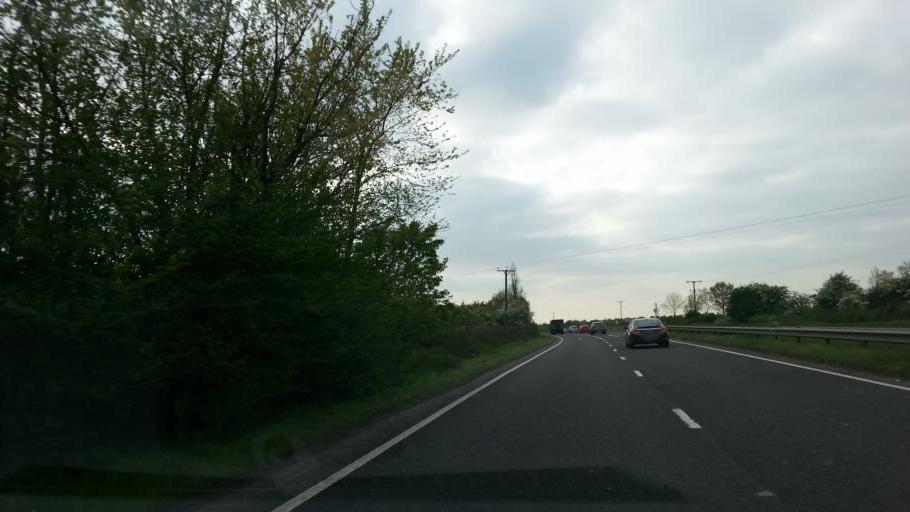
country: GB
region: England
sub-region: Nottinghamshire
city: South Collingham
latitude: 53.0737
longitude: -0.6883
